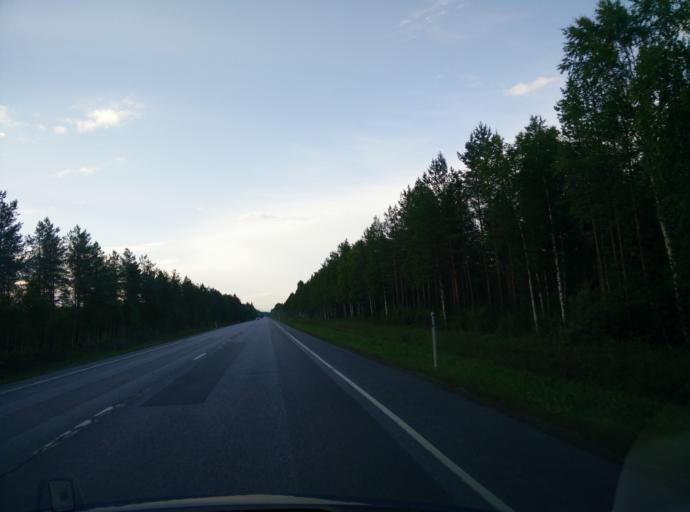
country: FI
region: Northern Ostrobothnia
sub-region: Haapavesi-Siikalatva
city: Pulkkila
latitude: 64.1317
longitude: 25.8000
